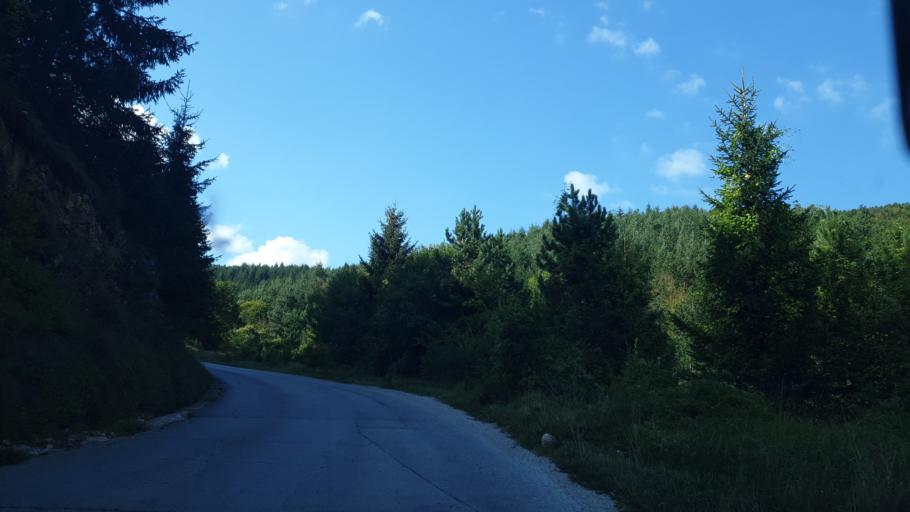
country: RS
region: Central Serbia
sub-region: Zlatiborski Okrug
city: Nova Varos
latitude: 43.4223
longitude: 19.9234
